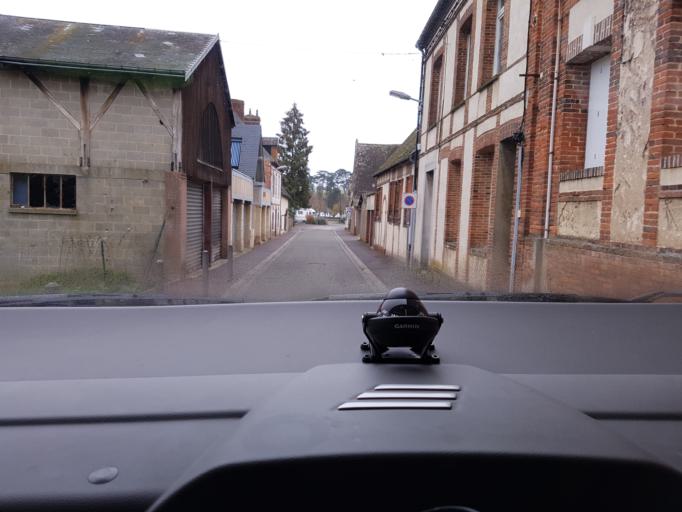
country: FR
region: Haute-Normandie
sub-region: Departement de l'Eure
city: Rugles
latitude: 48.8225
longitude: 0.7109
